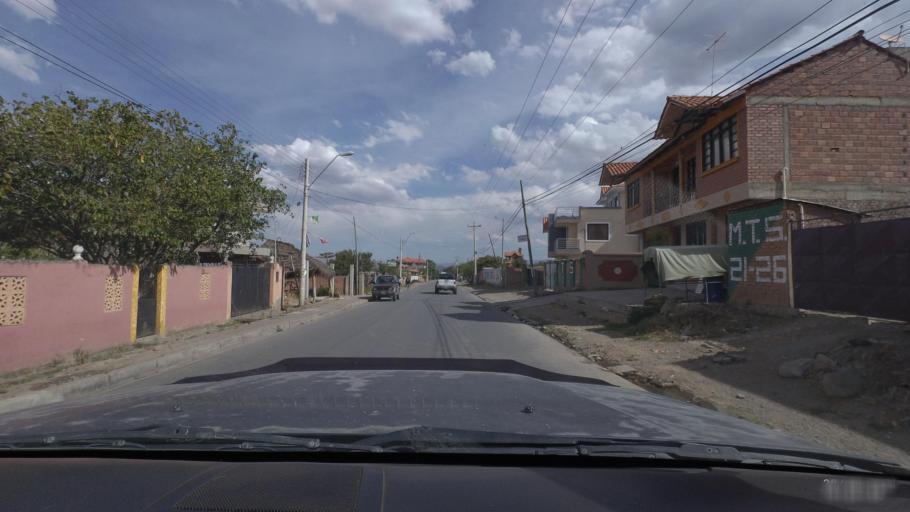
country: BO
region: Cochabamba
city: Cochabamba
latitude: -17.3261
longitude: -66.2822
